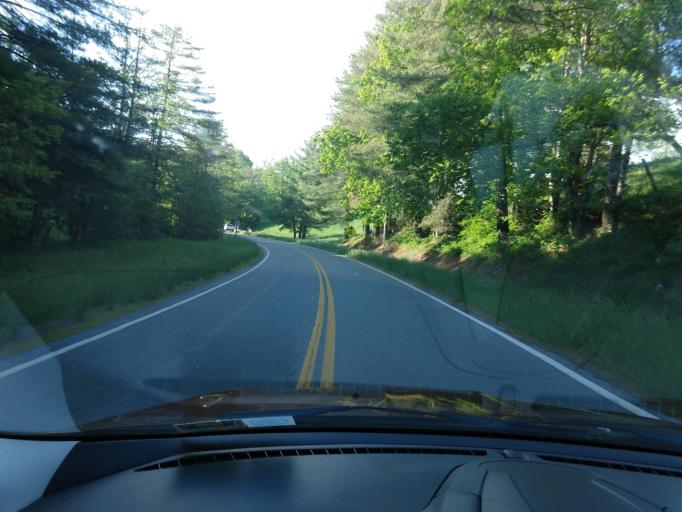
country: US
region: Virginia
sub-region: City of Galax
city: Galax
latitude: 36.7474
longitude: -80.9868
